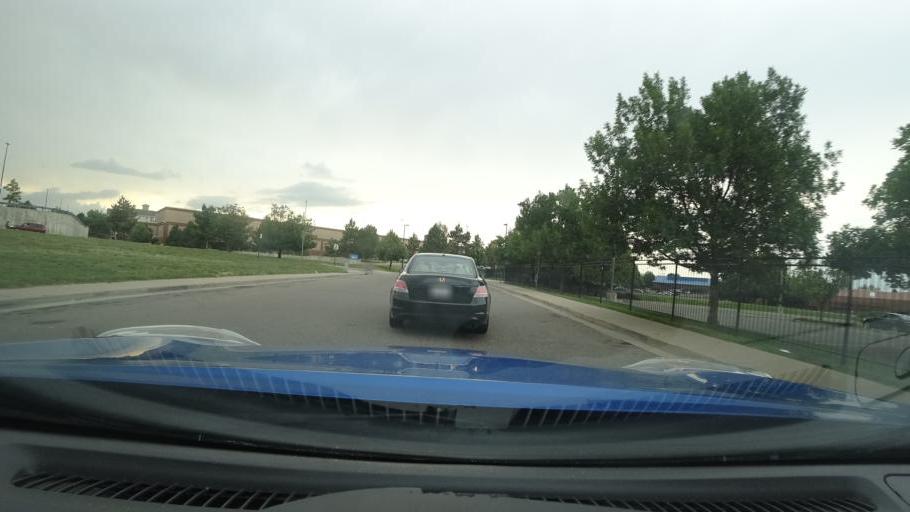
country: US
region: Colorado
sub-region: Adams County
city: Aurora
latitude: 39.7014
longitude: -104.8244
